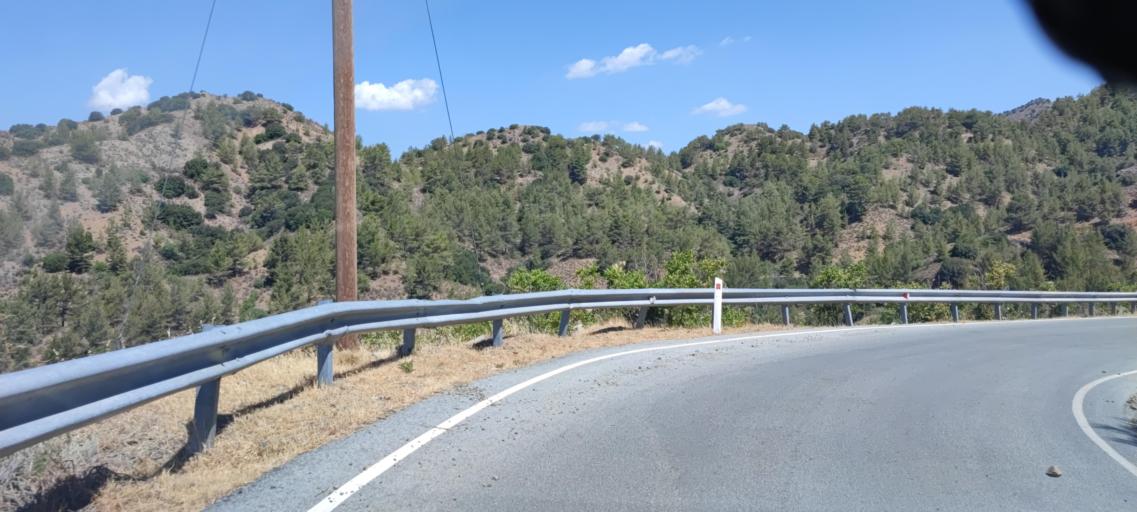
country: CY
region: Lefkosia
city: Kakopetria
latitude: 34.9258
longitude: 32.8051
